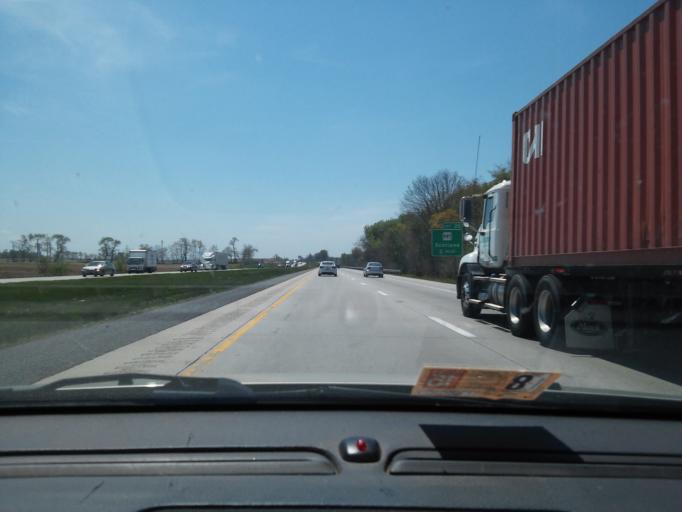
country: US
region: Pennsylvania
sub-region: Franklin County
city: Scotland
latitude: 39.9905
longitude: -77.5617
